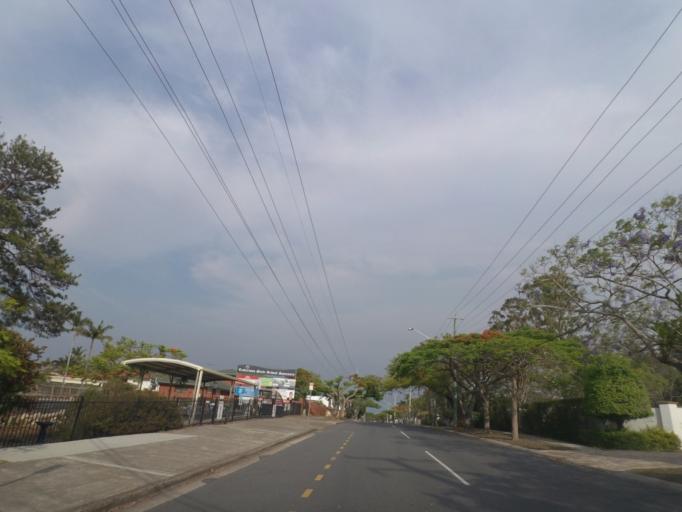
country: AU
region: Queensland
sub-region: Brisbane
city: Robertson
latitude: -27.5656
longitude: 153.0564
